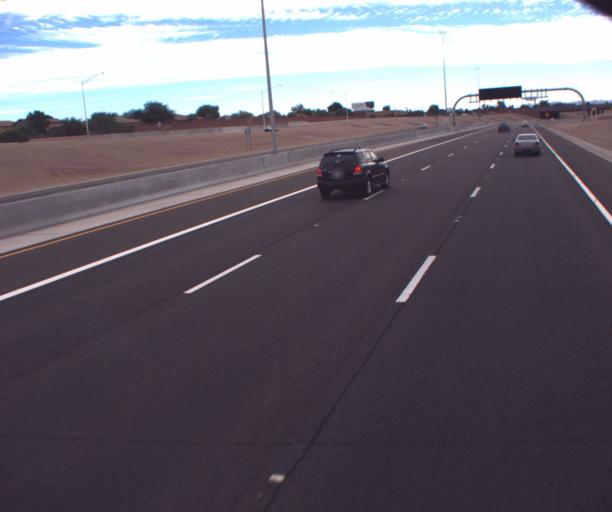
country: US
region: Arizona
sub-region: Pinal County
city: Apache Junction
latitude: 33.4205
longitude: -111.6364
